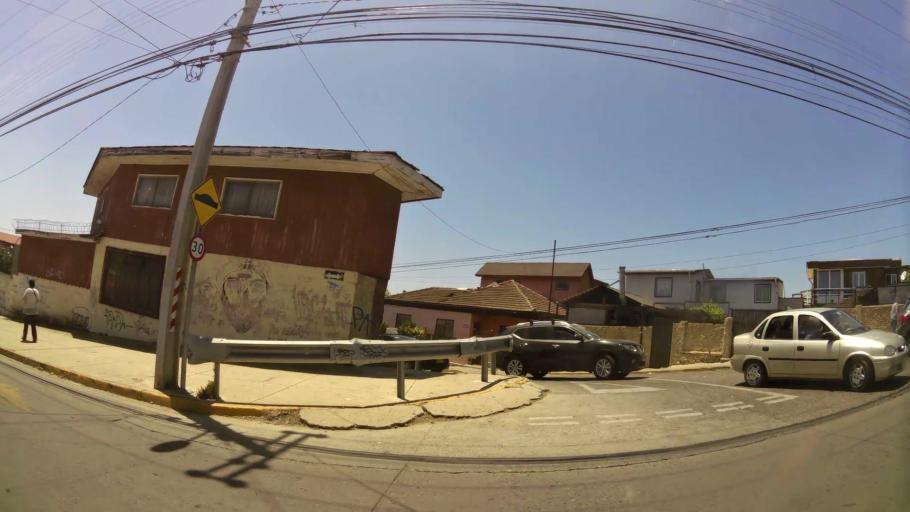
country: CL
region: Valparaiso
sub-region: Provincia de Valparaiso
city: Valparaiso
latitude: -33.0357
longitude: -71.6424
